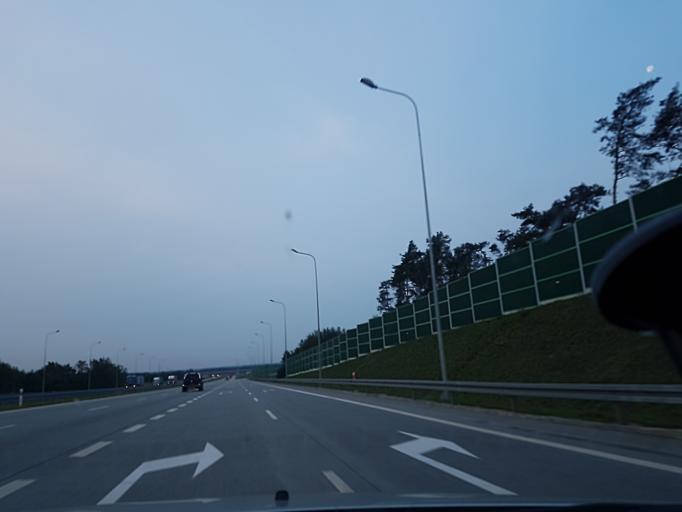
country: PL
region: Lodz Voivodeship
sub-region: Powiat lodzki wschodni
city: Tuszyn
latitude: 51.6482
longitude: 19.5757
